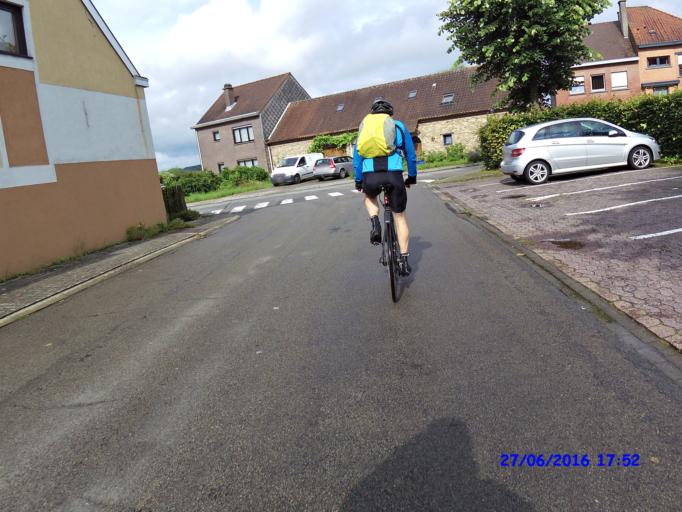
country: BE
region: Flanders
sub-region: Provincie Vlaams-Brabant
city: Ternat
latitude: 50.8765
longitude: 4.1302
